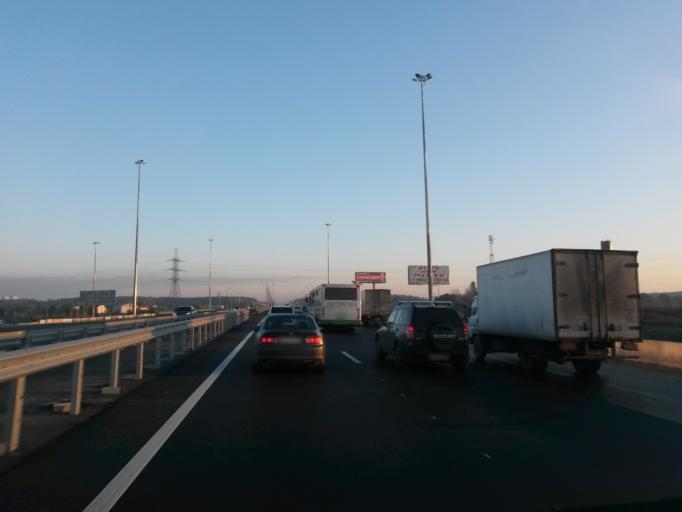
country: RU
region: Moskovskaya
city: Shcherbinka
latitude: 55.4804
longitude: 37.6147
